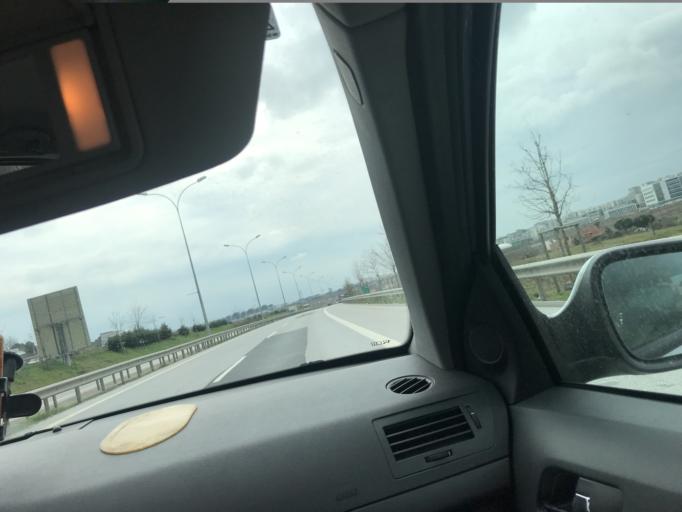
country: TR
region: Istanbul
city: Sultanbeyli
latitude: 40.9259
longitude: 29.3255
